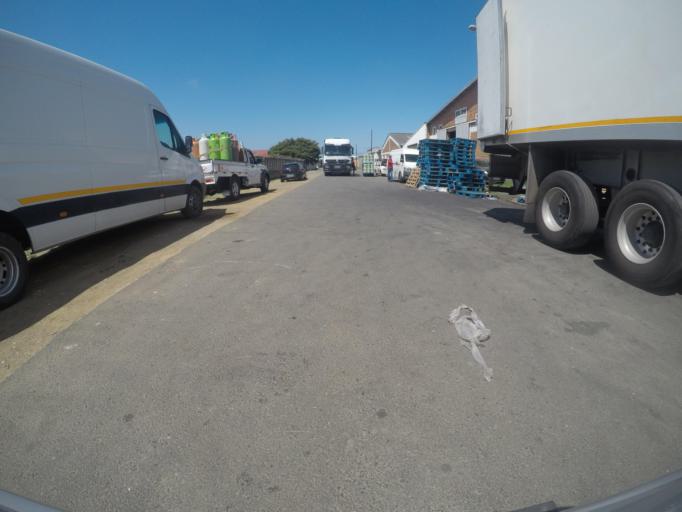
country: ZA
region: Eastern Cape
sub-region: Buffalo City Metropolitan Municipality
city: East London
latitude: -33.0083
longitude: 27.9116
